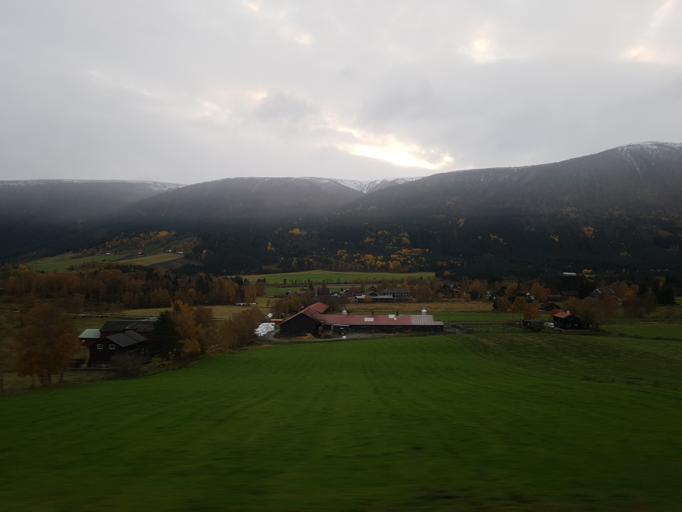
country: NO
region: Oppland
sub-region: Dovre
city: Dovre
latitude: 61.9934
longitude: 9.2410
